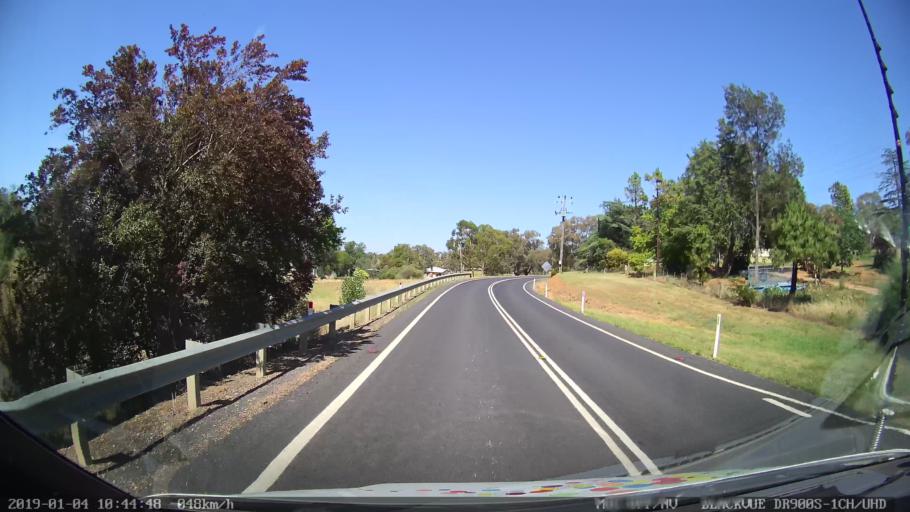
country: AU
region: New South Wales
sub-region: Cabonne
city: Molong
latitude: -33.2886
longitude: 148.7341
